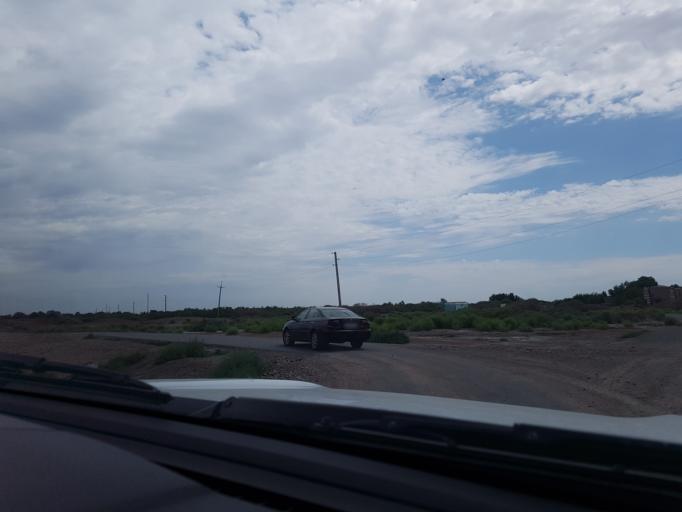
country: TM
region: Dasoguz
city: Koeneuergench
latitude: 42.2942
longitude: 59.1443
